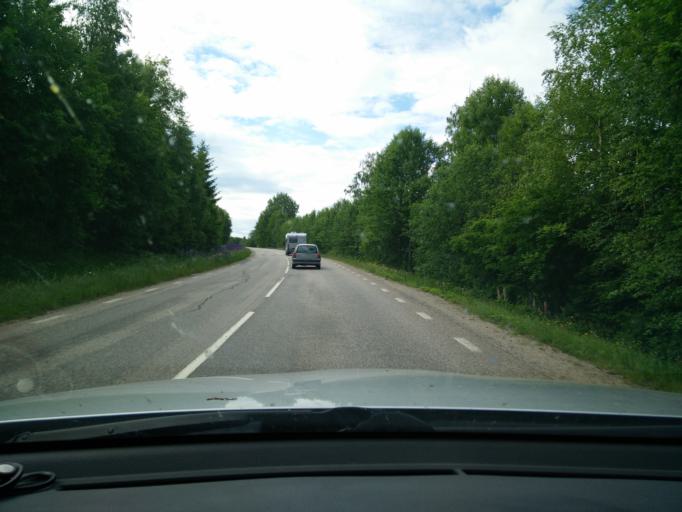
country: SE
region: Gaevleborg
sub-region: Nordanstigs Kommun
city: Bergsjoe
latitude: 61.9679
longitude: 17.0598
